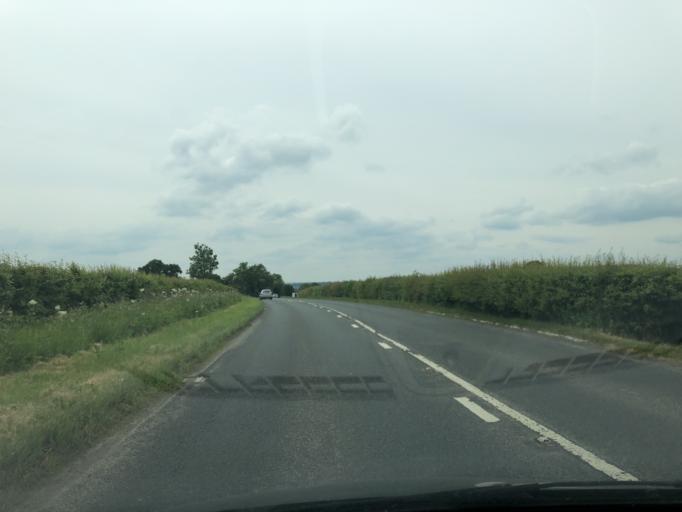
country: GB
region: England
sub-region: North Yorkshire
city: Great Habton
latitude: 54.2639
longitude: -0.9011
